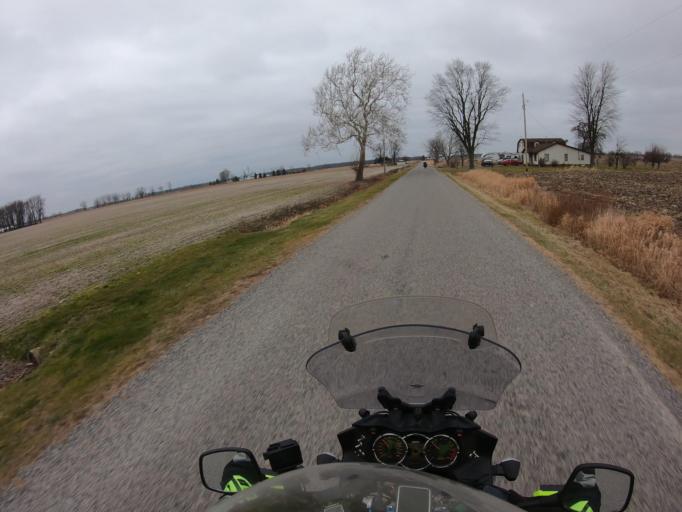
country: US
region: Michigan
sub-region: Saginaw County
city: Saint Charles
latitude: 43.2577
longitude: -84.0802
